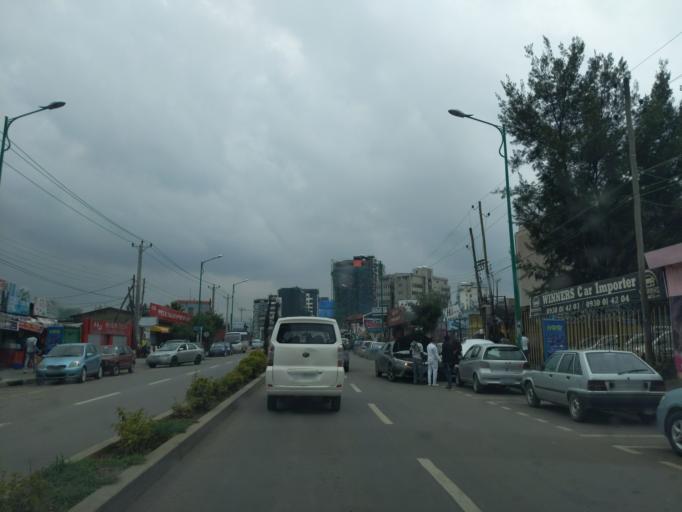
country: ET
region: Adis Abeba
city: Addis Ababa
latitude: 8.9976
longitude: 38.7668
